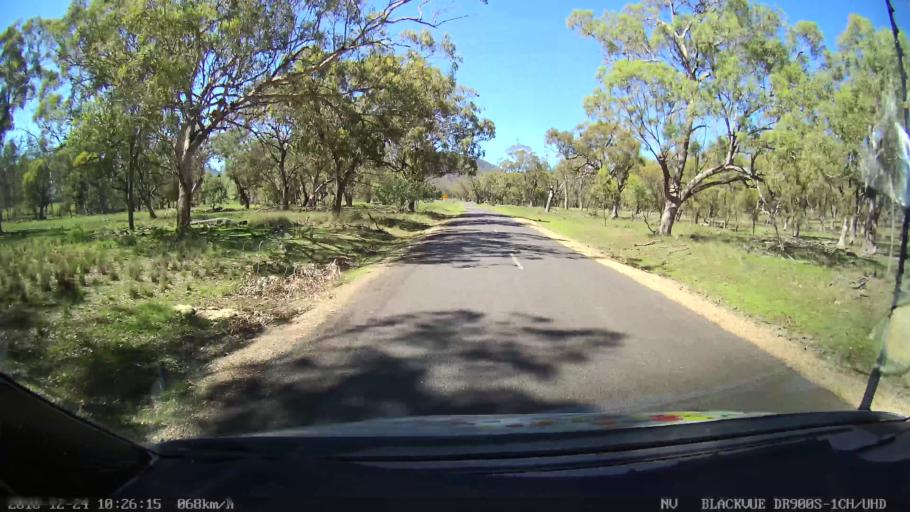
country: AU
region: New South Wales
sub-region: Liverpool Plains
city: Quirindi
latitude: -31.8075
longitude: 150.5278
